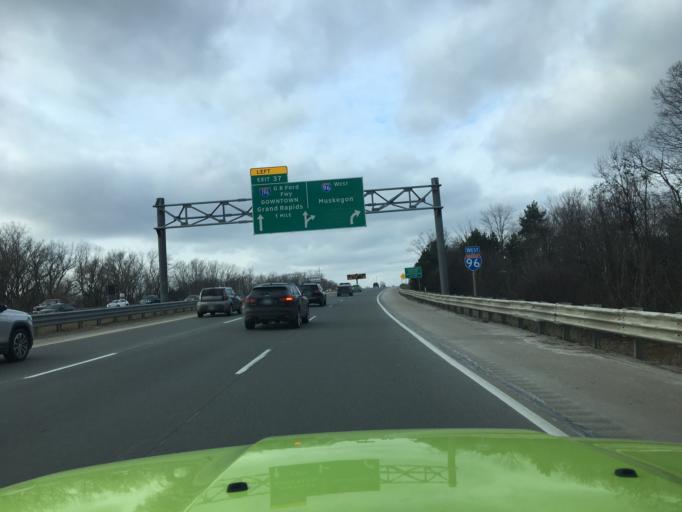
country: US
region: Michigan
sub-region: Kent County
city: East Grand Rapids
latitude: 42.9662
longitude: -85.5829
